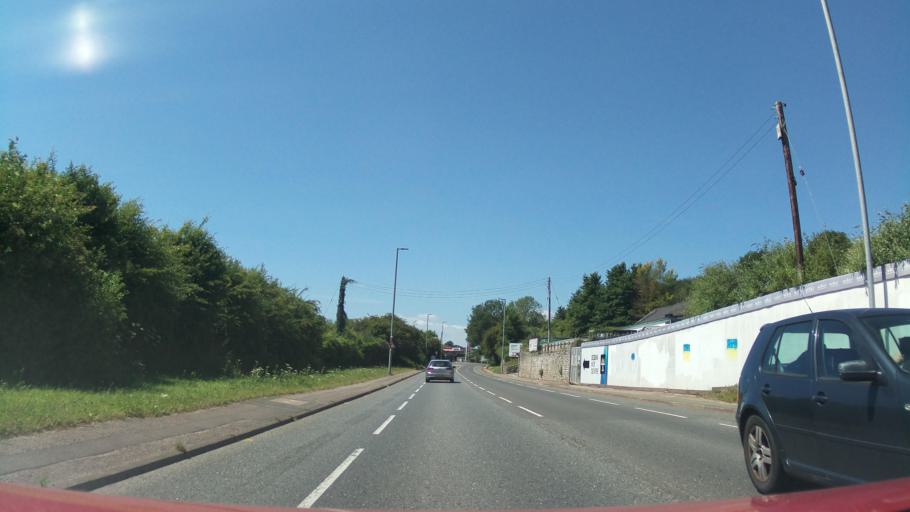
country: GB
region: England
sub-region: Devon
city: Kingskerswell
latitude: 50.4892
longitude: -3.5732
